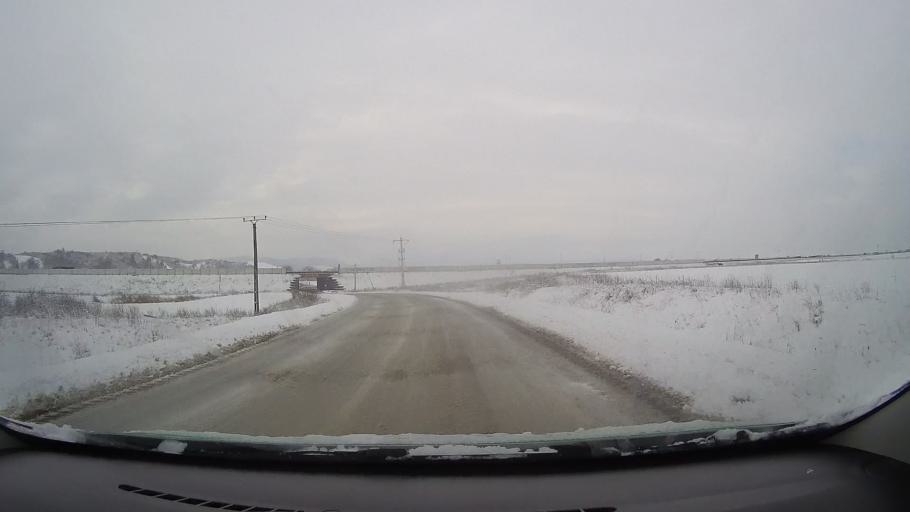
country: RO
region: Alba
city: Vurpar
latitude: 45.9693
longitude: 23.4794
